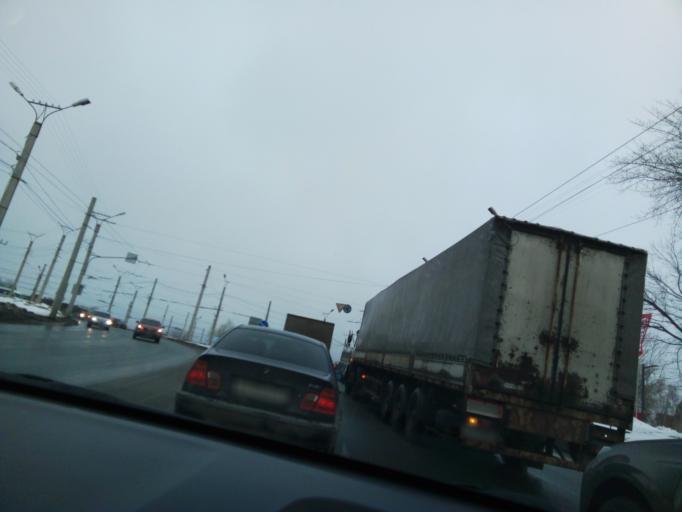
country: RU
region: Chuvashia
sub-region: Cheboksarskiy Rayon
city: Cheboksary
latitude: 56.1271
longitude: 47.2139
